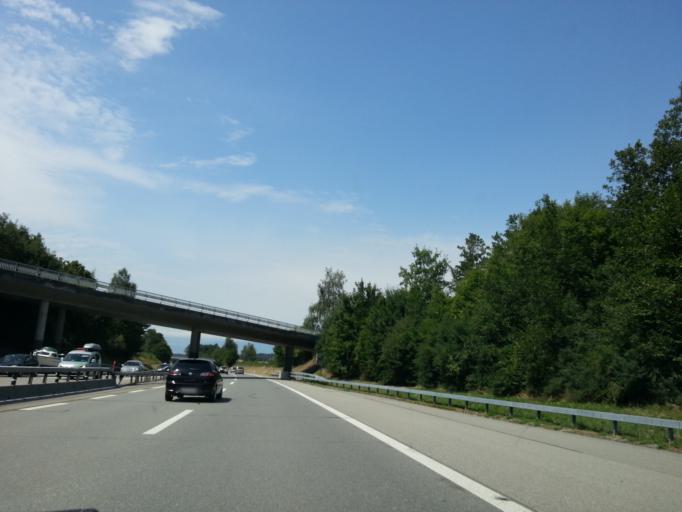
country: CH
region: Bern
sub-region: Bern-Mittelland District
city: Muhleberg
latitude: 46.9579
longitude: 7.2978
